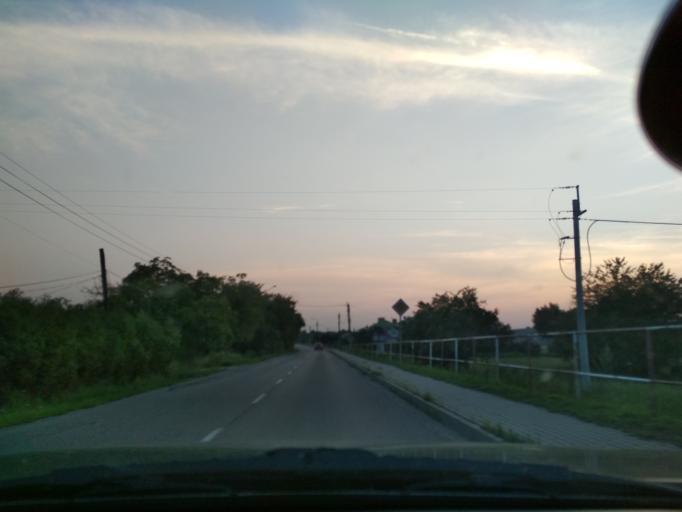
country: PL
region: Silesian Voivodeship
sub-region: Powiat zawiercianski
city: Pilica
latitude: 50.4699
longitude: 19.7279
